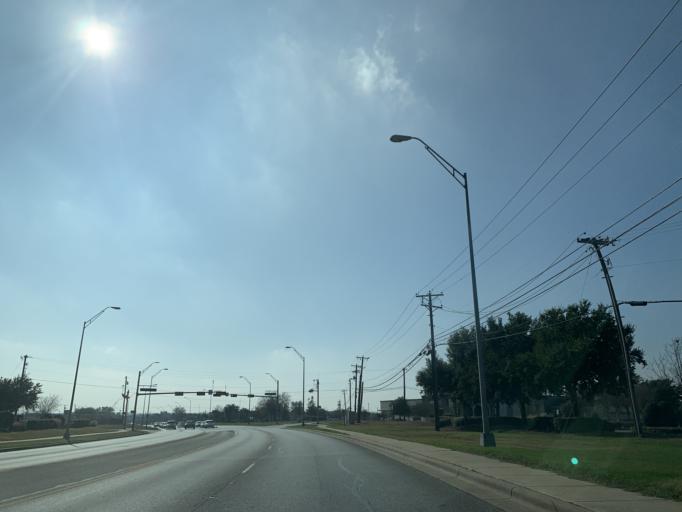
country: US
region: Texas
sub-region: Williamson County
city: Round Rock
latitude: 30.5221
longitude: -97.6553
